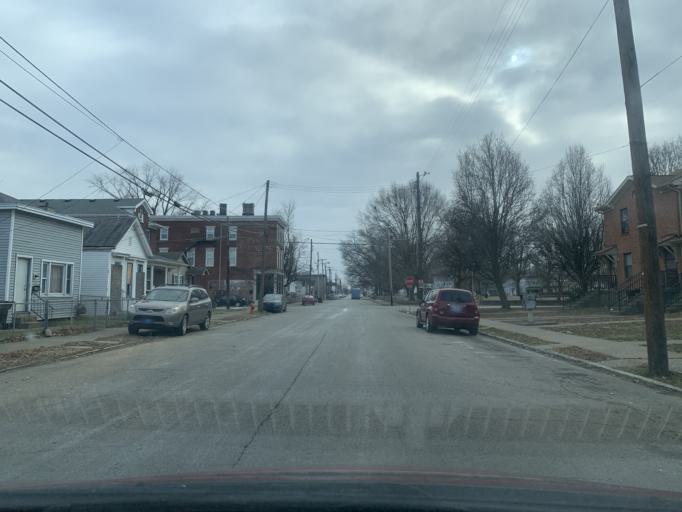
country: US
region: Kentucky
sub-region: Jefferson County
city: Louisville
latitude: 38.2626
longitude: -85.7808
